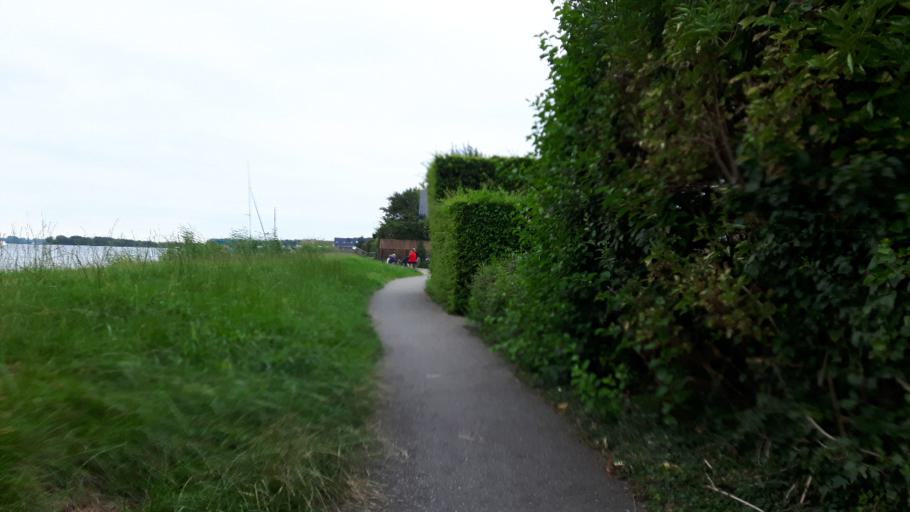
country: NL
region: South Holland
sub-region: Gemeente Kaag en Braassem
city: Oude Wetering
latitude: 52.1909
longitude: 4.6291
